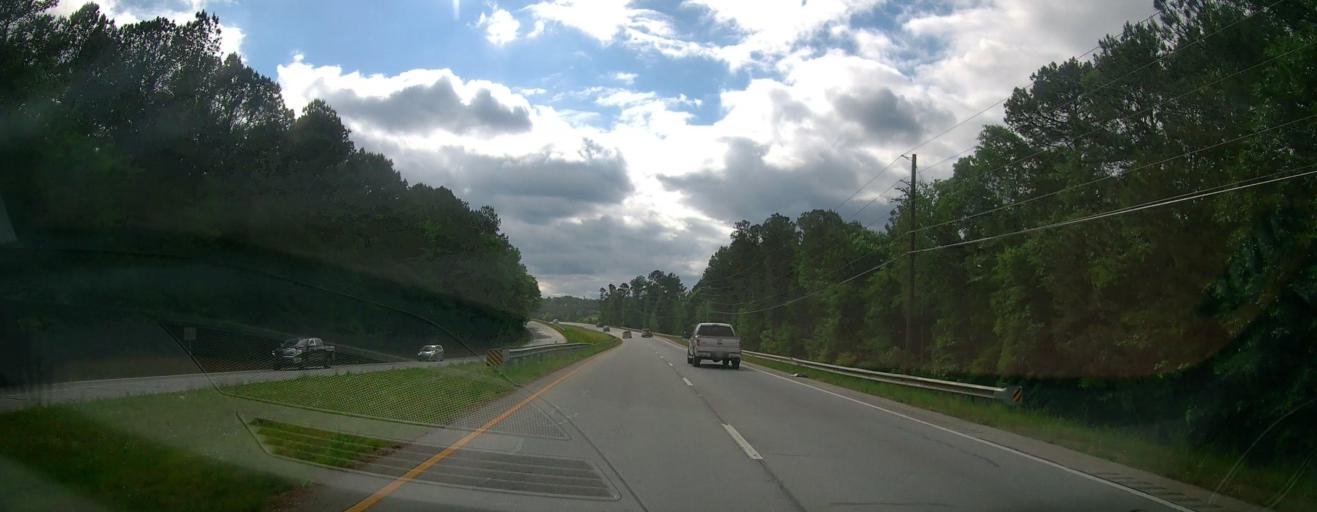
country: US
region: Georgia
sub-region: Walton County
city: Monroe
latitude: 33.8065
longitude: -83.7672
